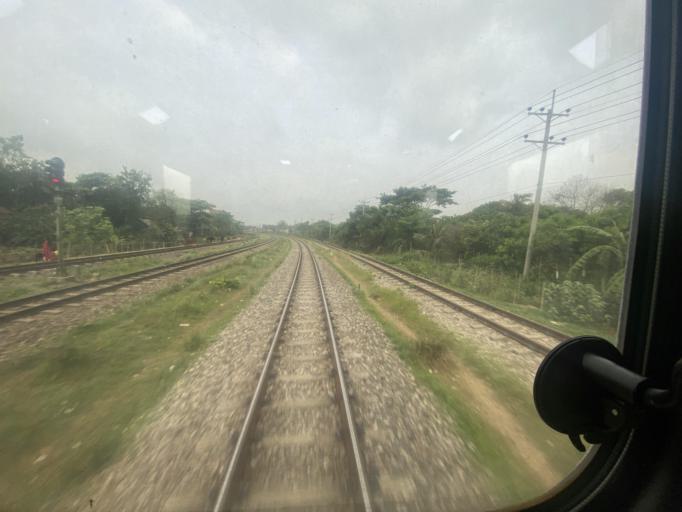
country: BD
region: Dhaka
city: Tungi
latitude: 23.9363
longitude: 90.4735
